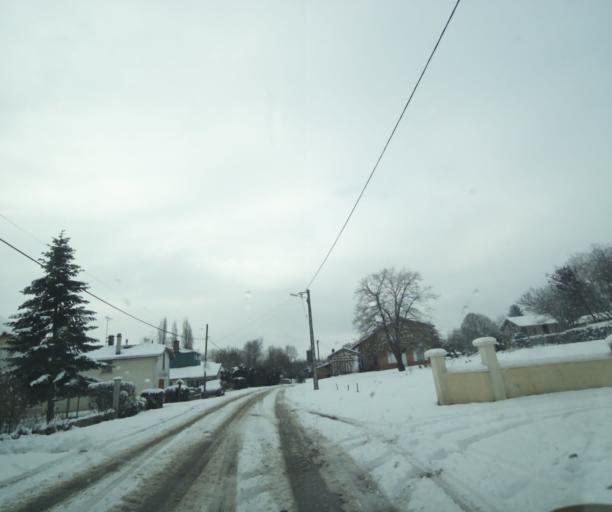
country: FR
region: Champagne-Ardenne
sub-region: Departement de la Haute-Marne
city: Montier-en-Der
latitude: 48.5183
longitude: 4.7006
